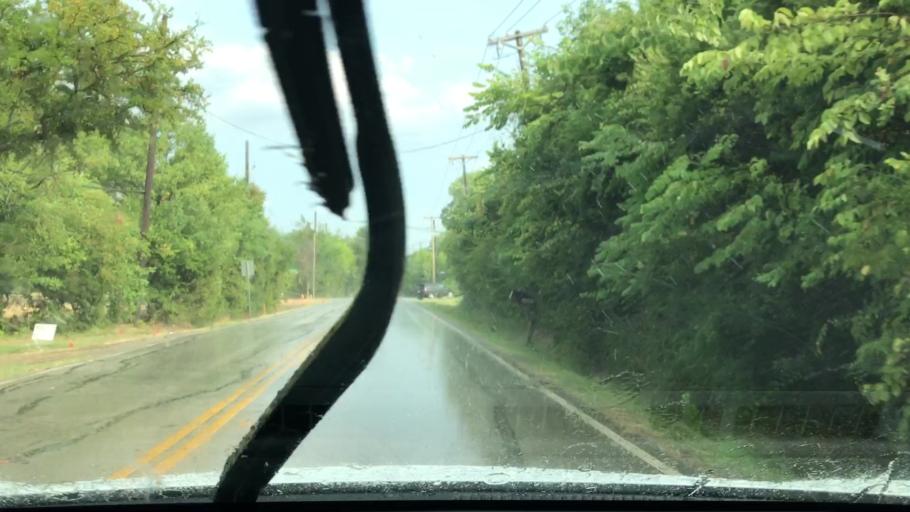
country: US
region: Texas
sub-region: Collin County
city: Wylie
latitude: 32.9566
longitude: -96.5269
